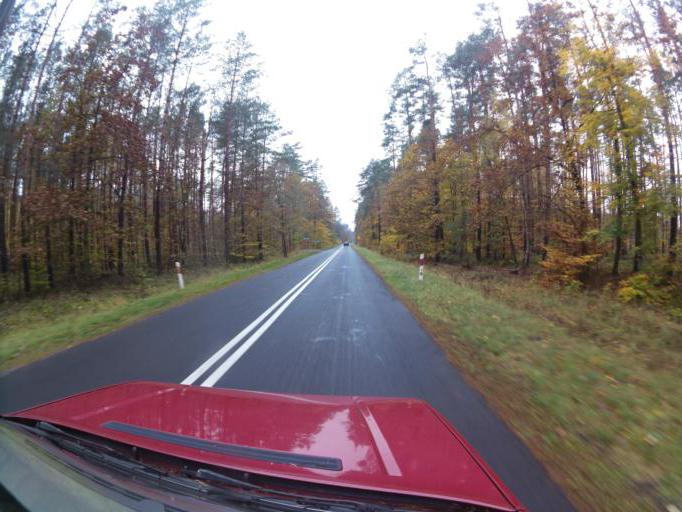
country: PL
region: West Pomeranian Voivodeship
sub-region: Powiat policki
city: Dobra
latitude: 53.5986
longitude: 14.3417
